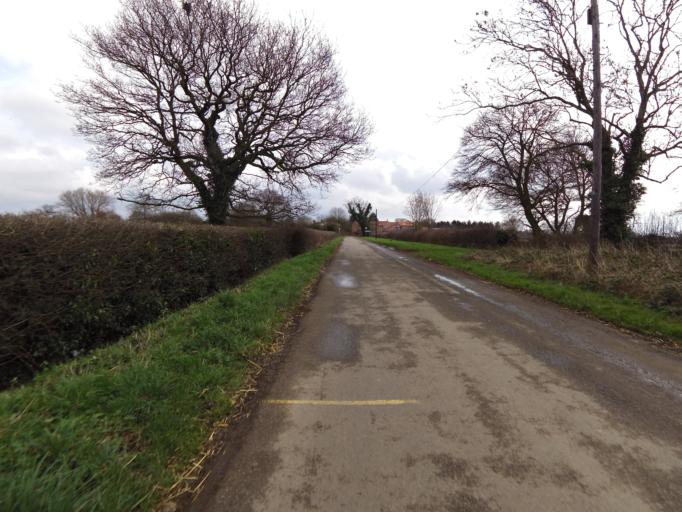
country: GB
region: England
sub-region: Doncaster
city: Moss
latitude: 53.6065
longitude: -1.0725
